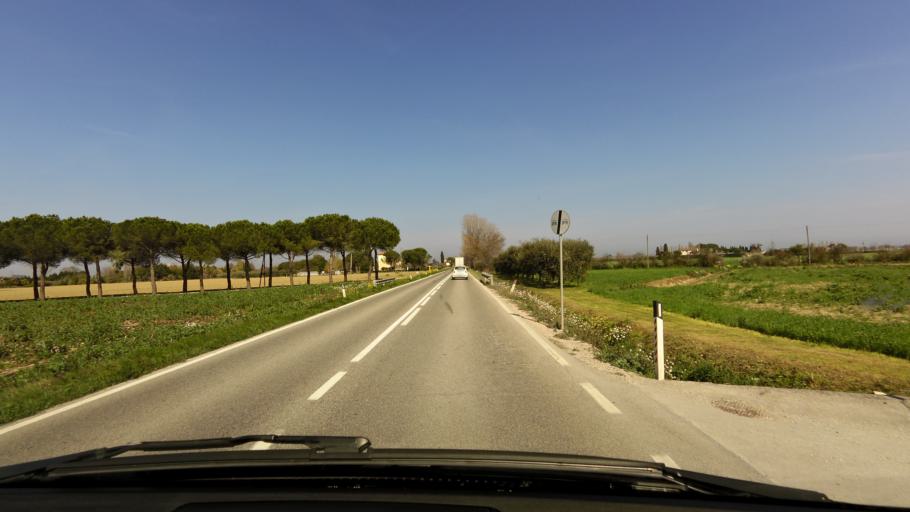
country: IT
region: The Marches
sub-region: Provincia di Macerata
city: Porto Recanati
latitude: 43.3981
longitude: 13.6521
